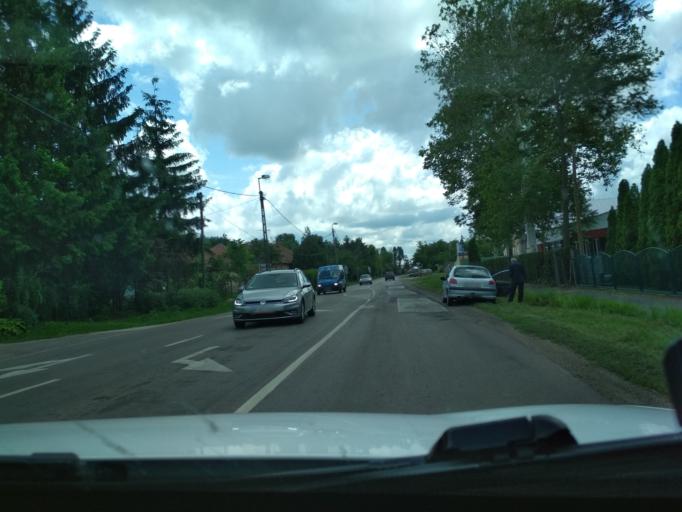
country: HU
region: Jasz-Nagykun-Szolnok
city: Tiszafured
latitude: 47.6072
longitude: 20.7625
